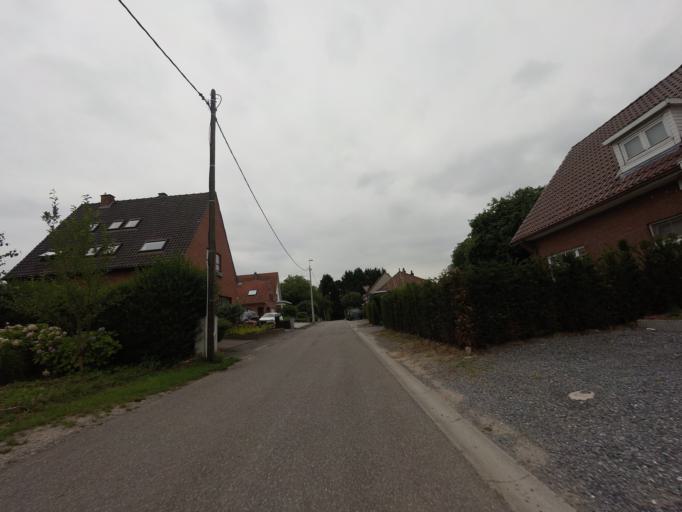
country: BE
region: Flanders
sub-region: Provincie Vlaams-Brabant
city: Grimbergen
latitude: 50.9313
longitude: 4.3836
